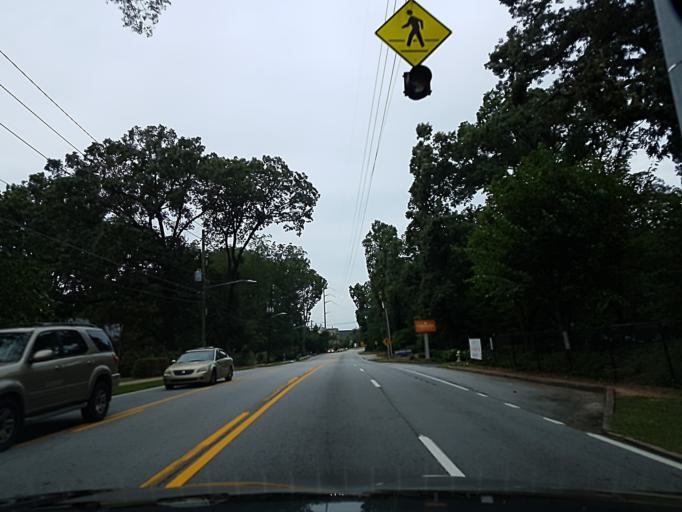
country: US
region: Georgia
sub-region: DeKalb County
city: Druid Hills
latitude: 33.7812
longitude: -84.3440
